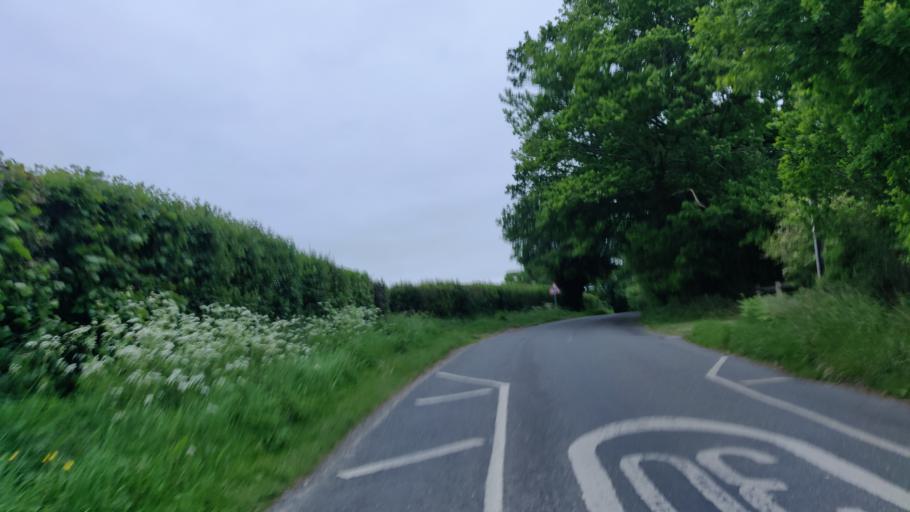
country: GB
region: England
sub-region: West Sussex
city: Southwater
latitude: 51.0255
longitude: -0.3593
